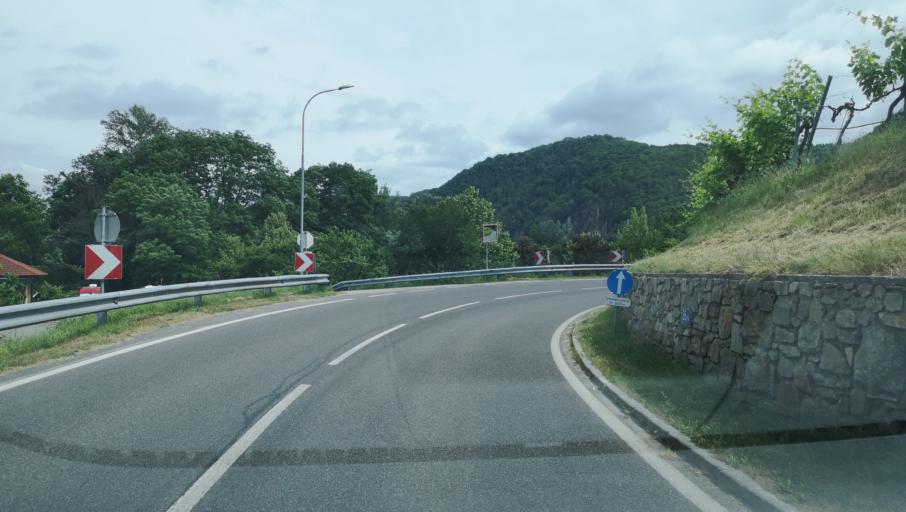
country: AT
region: Lower Austria
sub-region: Politischer Bezirk Krems
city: Durnstein
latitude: 48.3878
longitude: 15.5169
